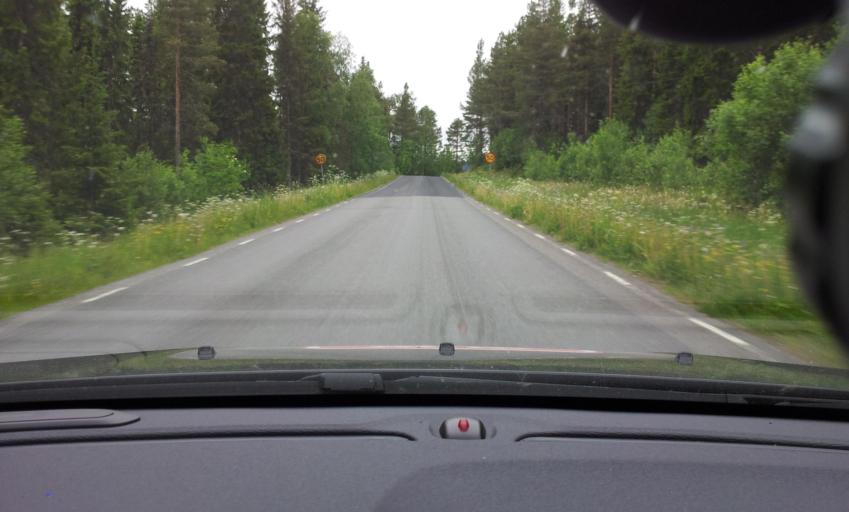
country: SE
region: Jaemtland
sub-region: Krokoms Kommun
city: Valla
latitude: 63.2849
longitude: 13.7736
